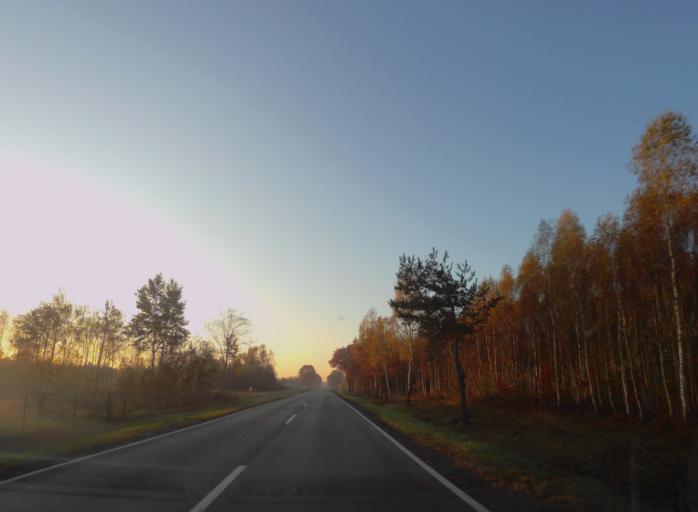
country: PL
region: Subcarpathian Voivodeship
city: Nowa Sarzyna
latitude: 50.3454
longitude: 22.3261
